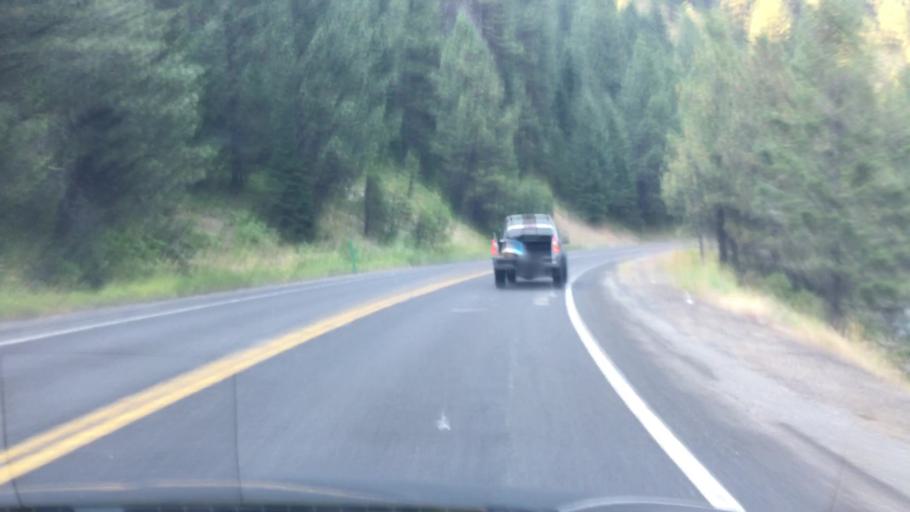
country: US
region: Idaho
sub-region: Valley County
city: Cascade
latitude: 44.2494
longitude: -116.0934
